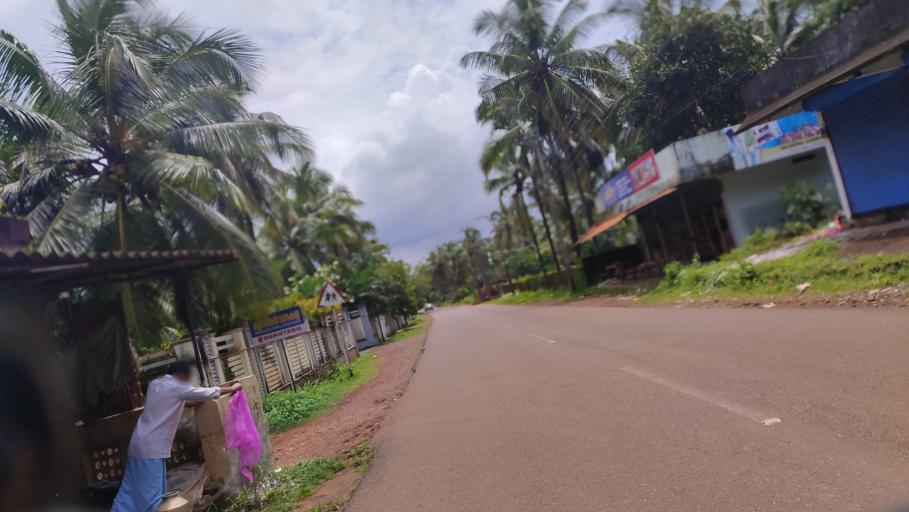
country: IN
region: Kerala
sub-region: Kasaragod District
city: Kannangad
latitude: 12.3929
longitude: 75.0508
